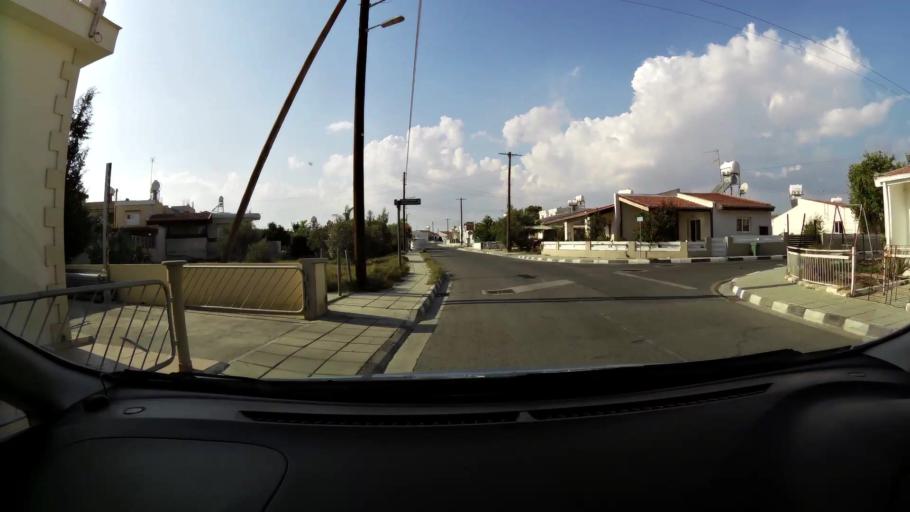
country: CY
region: Larnaka
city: Dhromolaxia
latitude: 34.8740
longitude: 33.5895
